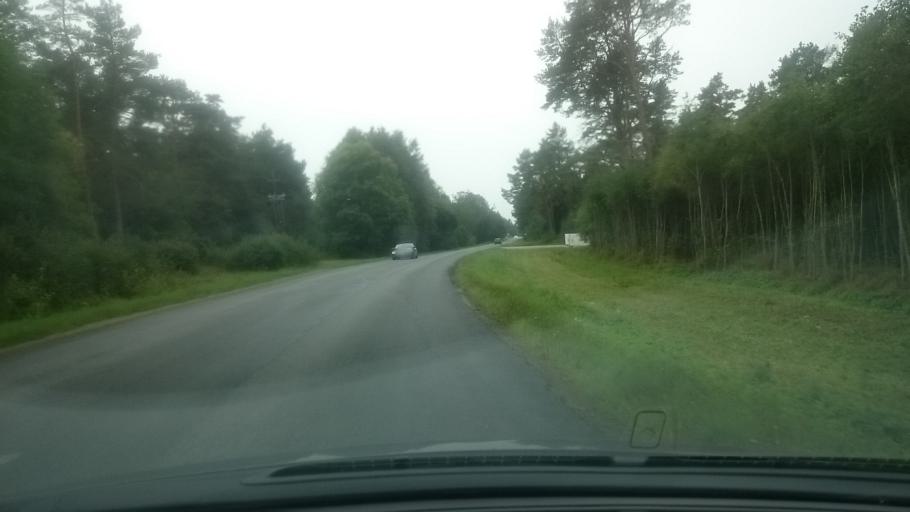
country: EE
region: Harju
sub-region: Raasiku vald
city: Raasiku
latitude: 59.4453
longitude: 25.1947
